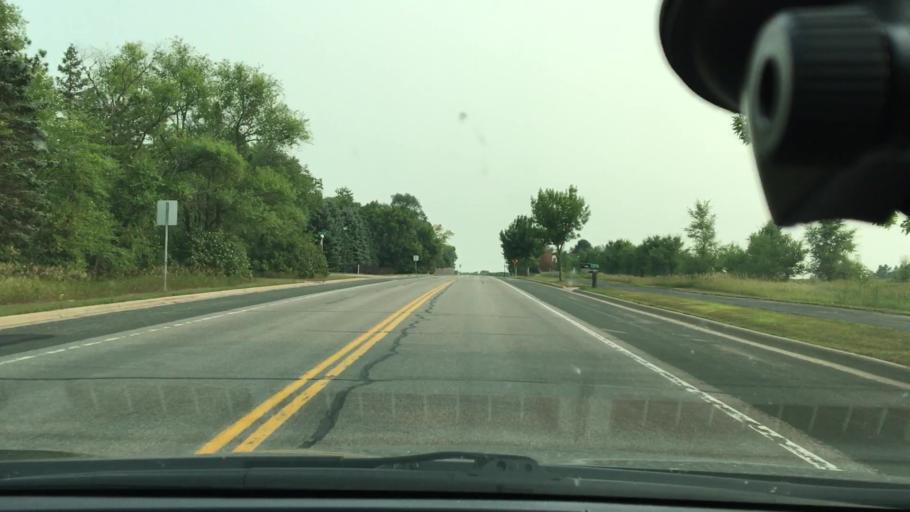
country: US
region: Minnesota
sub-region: Wright County
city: Otsego
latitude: 45.2555
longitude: -93.5913
